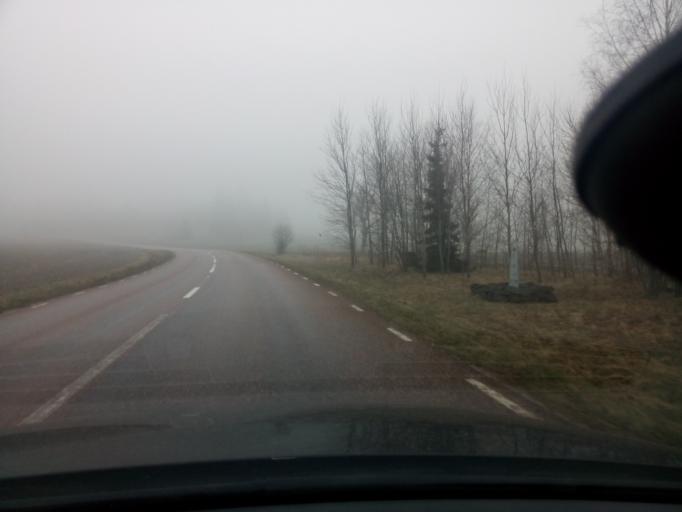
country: SE
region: Soedermanland
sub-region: Nykopings Kommun
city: Nykoping
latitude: 58.8216
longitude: 17.0736
